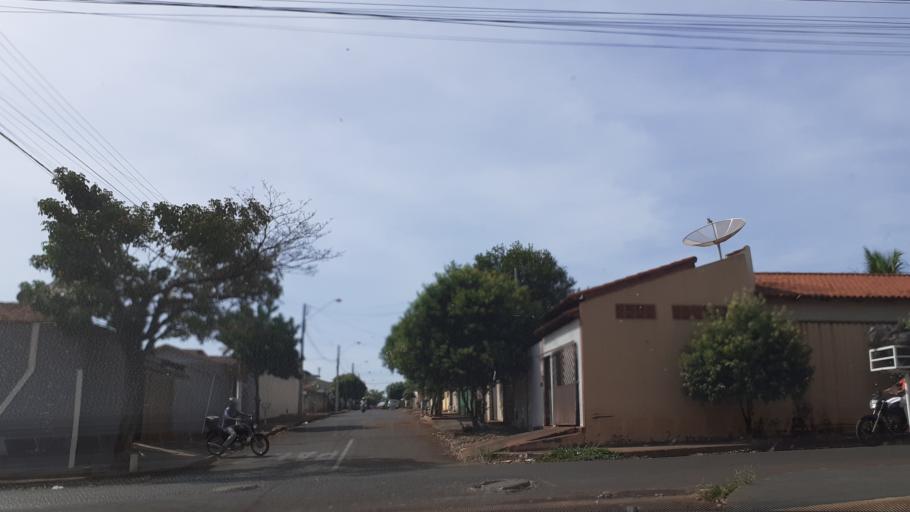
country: BR
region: Goias
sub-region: Itumbiara
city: Itumbiara
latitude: -18.4221
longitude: -49.2324
